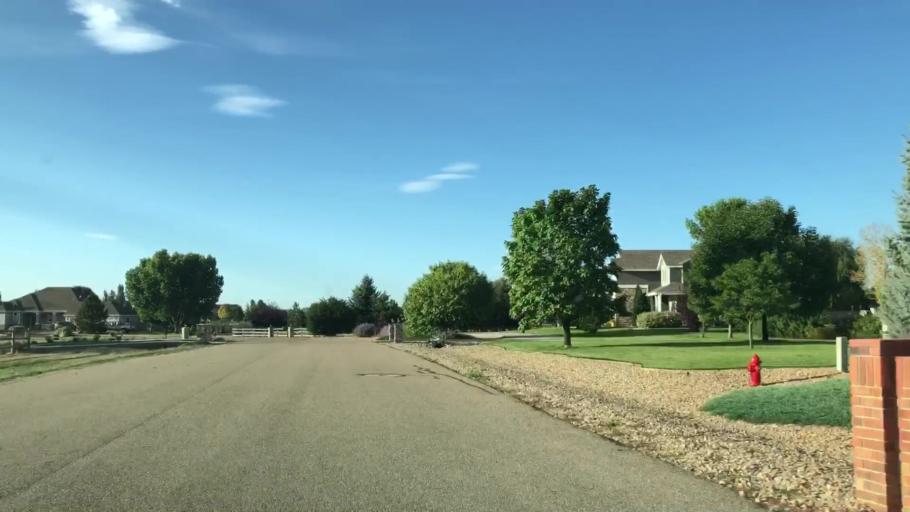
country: US
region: Colorado
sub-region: Weld County
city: Windsor
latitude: 40.4426
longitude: -104.9494
